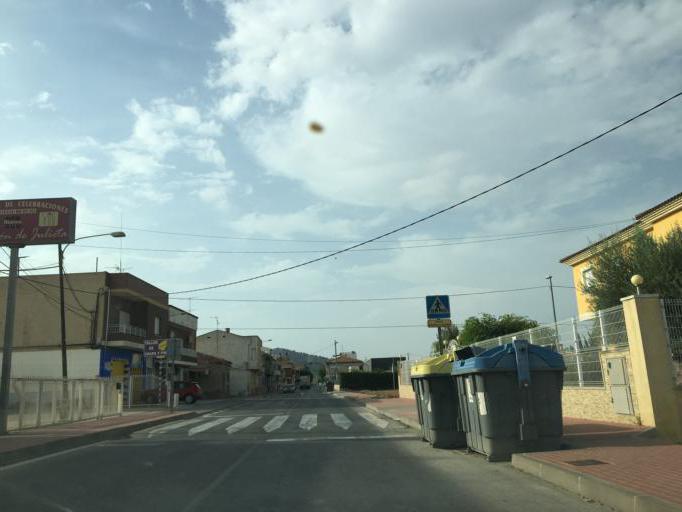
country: ES
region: Murcia
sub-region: Murcia
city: Murcia
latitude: 38.0119
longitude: -1.0815
